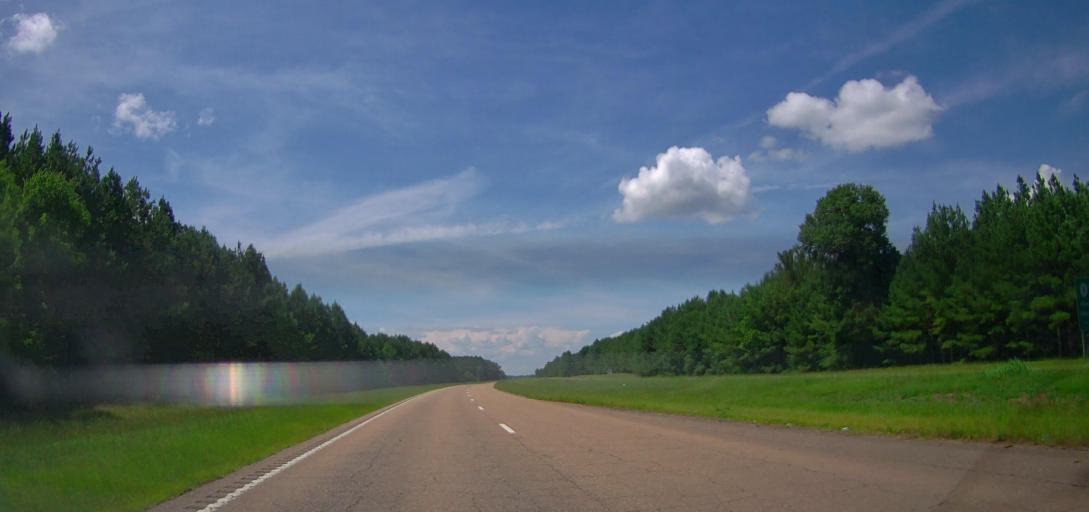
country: US
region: Mississippi
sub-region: Monroe County
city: Aberdeen
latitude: 33.8211
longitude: -88.5827
